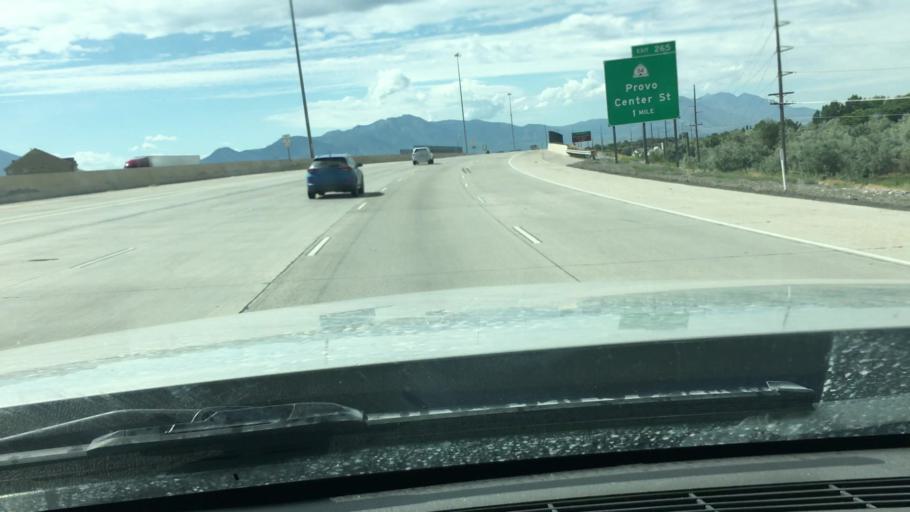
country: US
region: Utah
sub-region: Utah County
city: Provo
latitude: 40.2506
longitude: -111.6958
